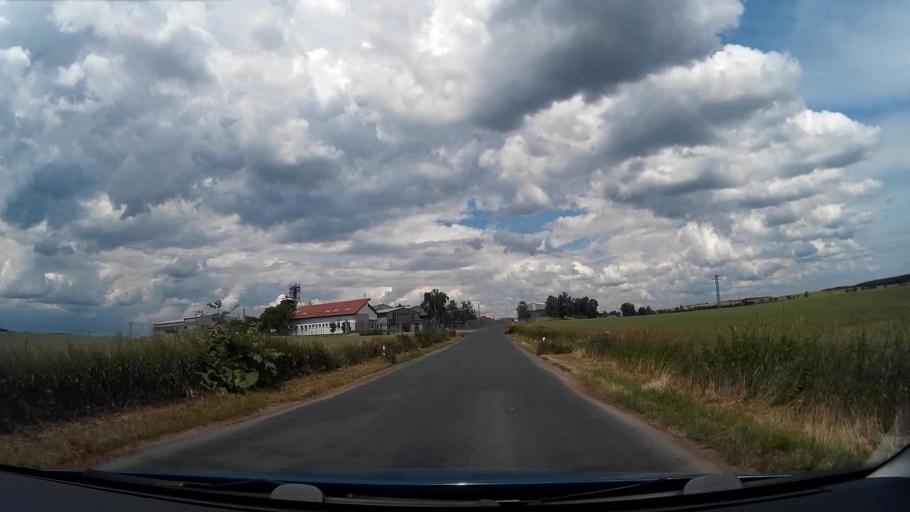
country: CZ
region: South Moravian
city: Orechov
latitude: 49.1028
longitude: 16.5250
